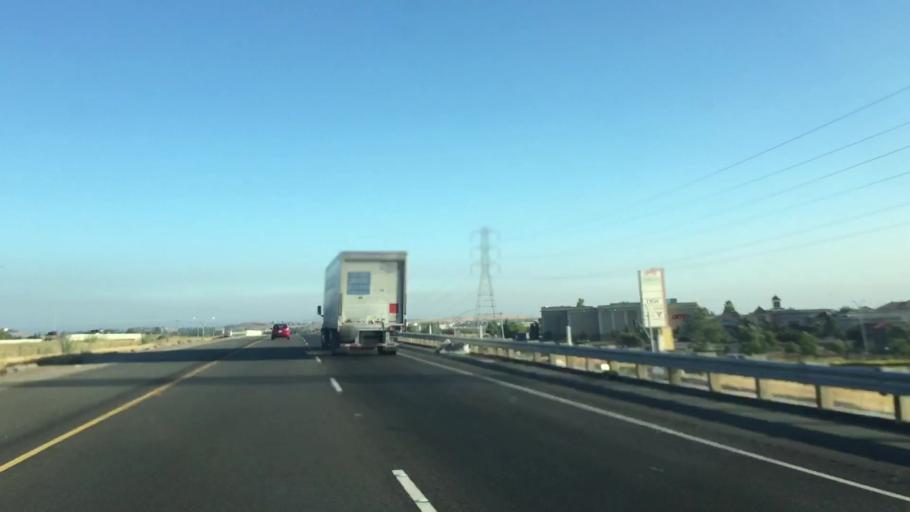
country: US
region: California
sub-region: Contra Costa County
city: Brentwood
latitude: 37.9423
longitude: -121.7408
